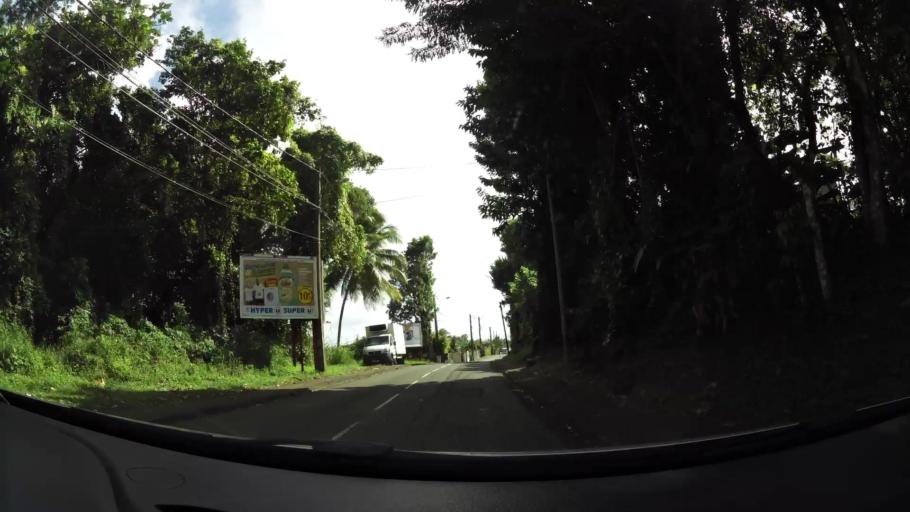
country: MQ
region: Martinique
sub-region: Martinique
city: Fort-de-France
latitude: 14.6393
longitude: -61.0595
